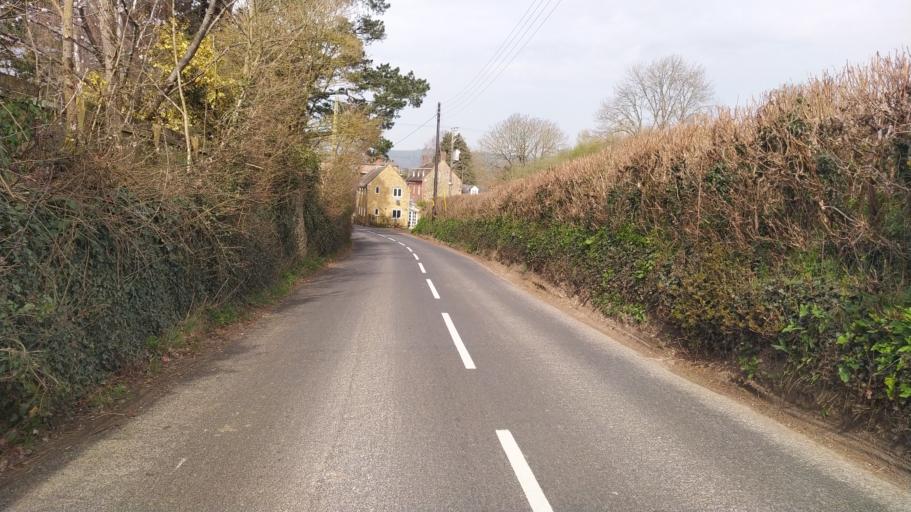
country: GB
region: England
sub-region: Dorset
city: Beaminster
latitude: 50.8061
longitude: -2.7333
